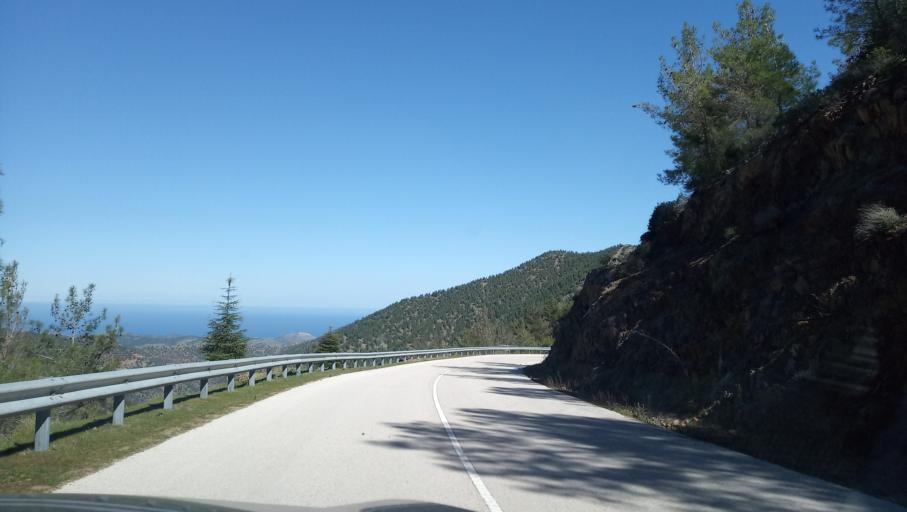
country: CY
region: Lefkosia
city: Lefka
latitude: 35.0716
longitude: 32.7623
